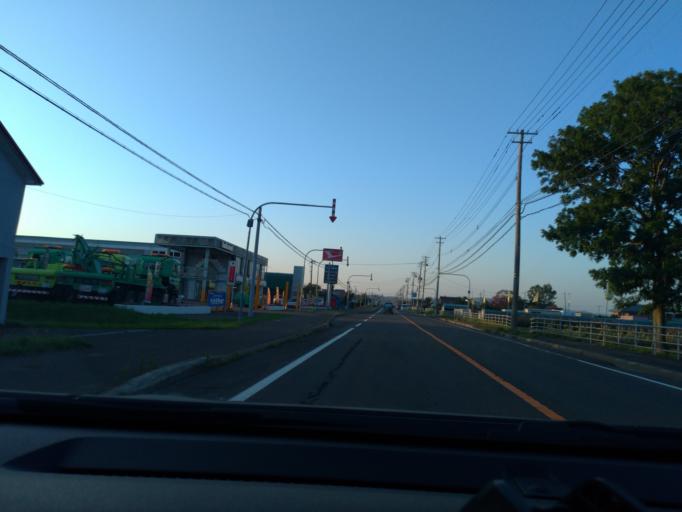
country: JP
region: Hokkaido
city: Tobetsu
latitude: 43.1999
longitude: 141.5220
